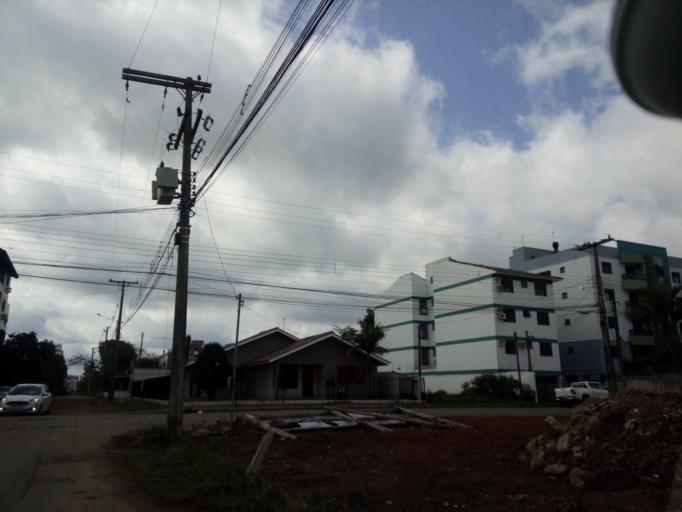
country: BR
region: Rio Grande do Sul
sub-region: Santa Maria
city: Santa Maria
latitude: -29.7040
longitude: -53.7249
